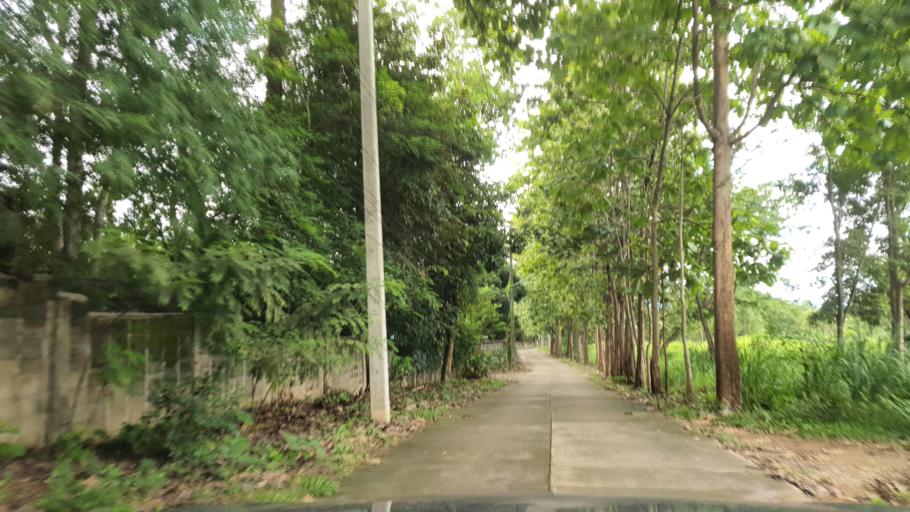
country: TH
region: Chiang Mai
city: Chiang Mai
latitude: 18.7815
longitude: 98.9496
